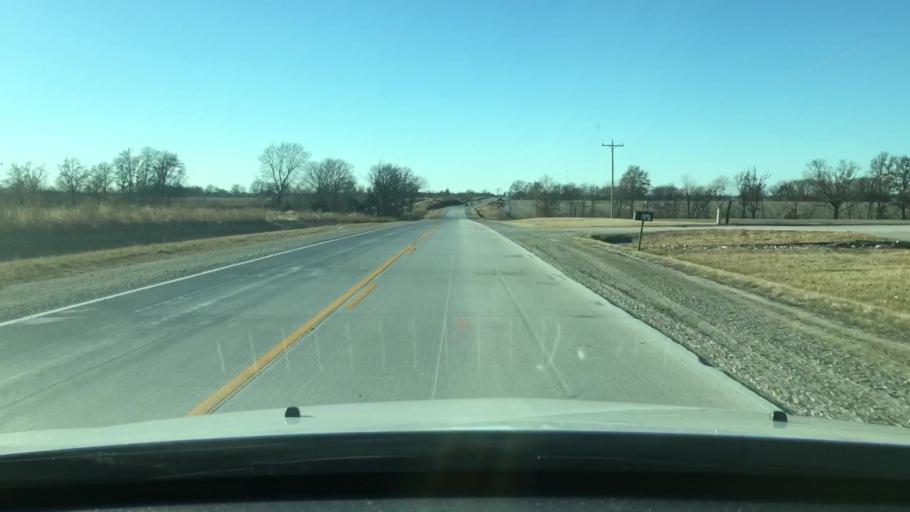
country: US
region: Missouri
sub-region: Boone County
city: Centralia
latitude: 39.2013
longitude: -92.0635
